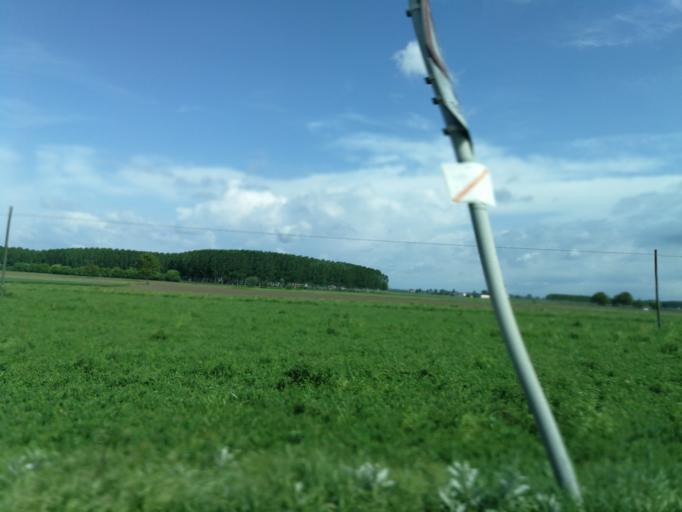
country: IT
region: Piedmont
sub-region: Provincia di Cuneo
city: Moretta
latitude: 44.7730
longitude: 7.5468
